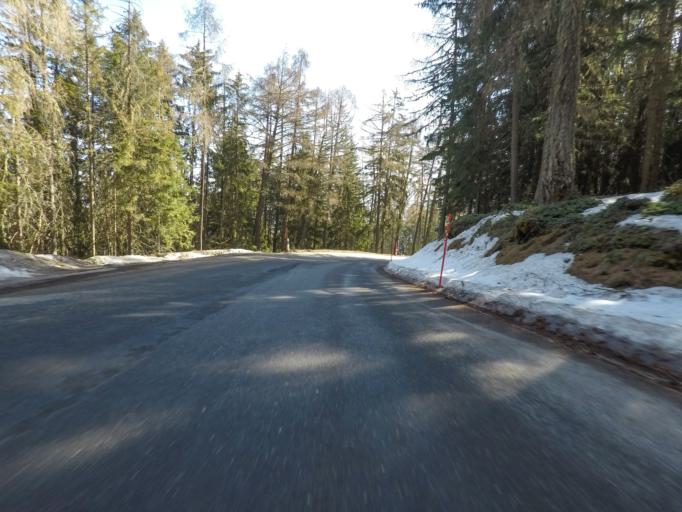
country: CH
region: Valais
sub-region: Herens District
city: Vex
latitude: 46.1943
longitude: 7.3842
